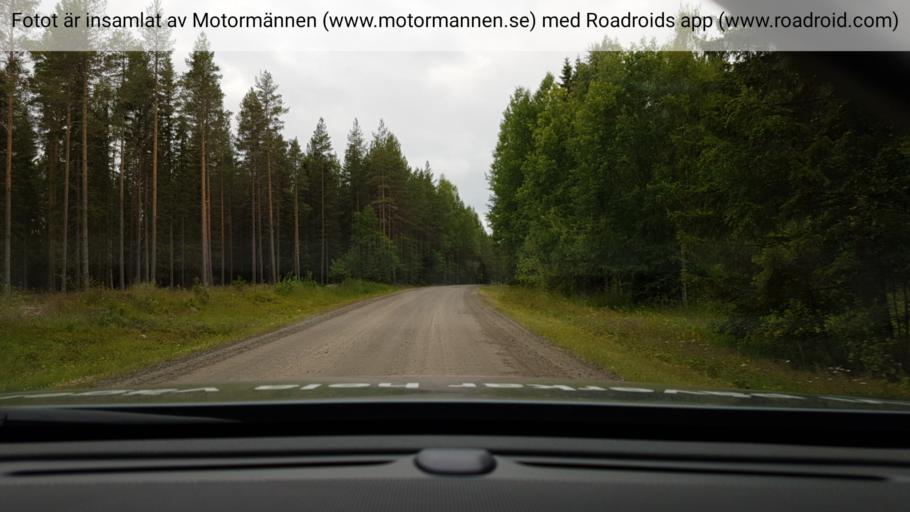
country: SE
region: Vaesterbotten
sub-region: Umea Kommun
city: Roback
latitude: 64.1117
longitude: 20.0923
